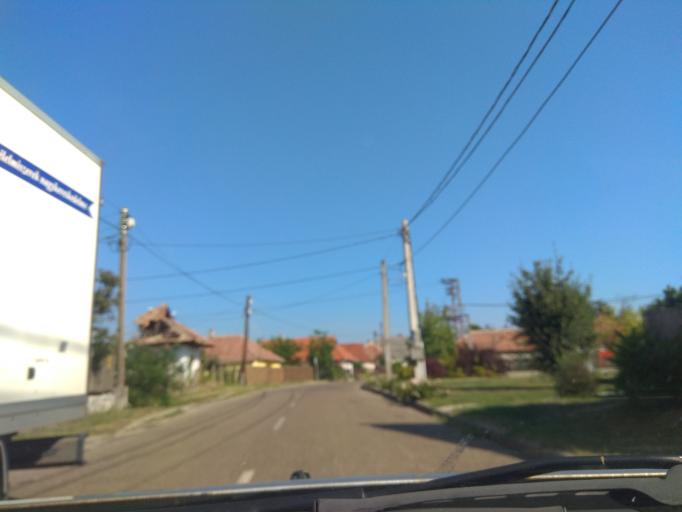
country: HU
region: Borsod-Abauj-Zemplen
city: Emod
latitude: 47.9460
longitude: 20.8121
